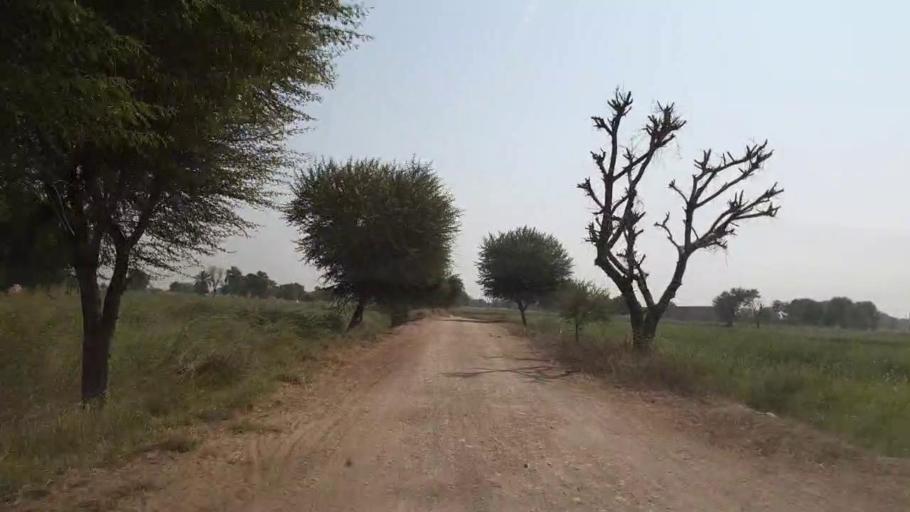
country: PK
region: Sindh
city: Mirpur Khas
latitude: 25.6472
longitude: 69.1152
